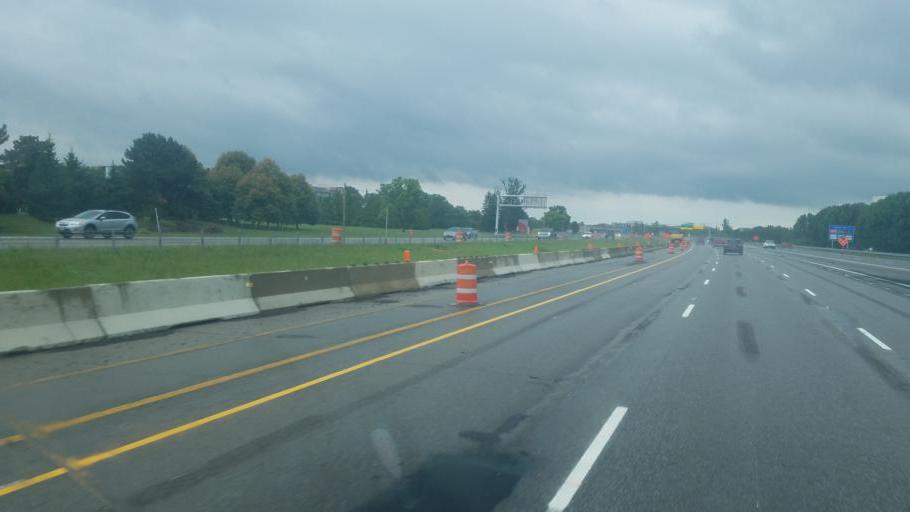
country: US
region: Ohio
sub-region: Franklin County
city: Dublin
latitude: 40.0909
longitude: -83.1384
